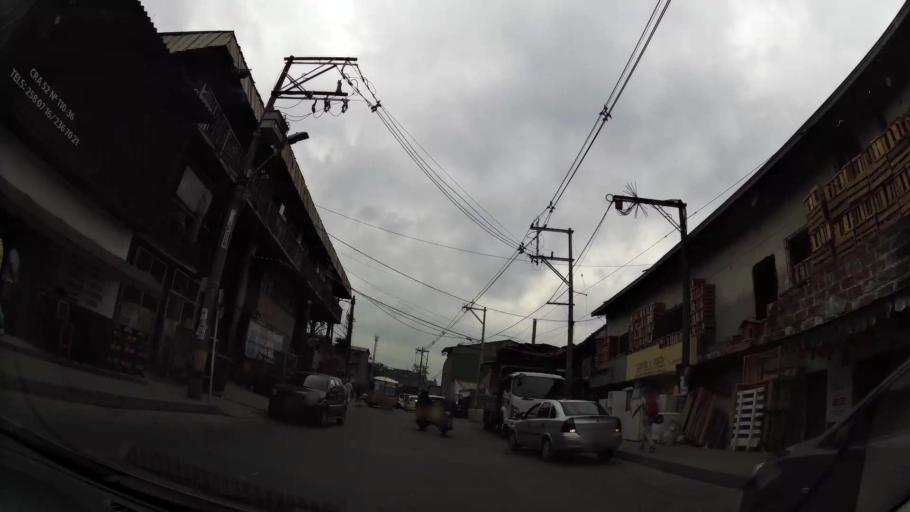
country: CO
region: Antioquia
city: Bello
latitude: 6.3027
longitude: -75.5562
